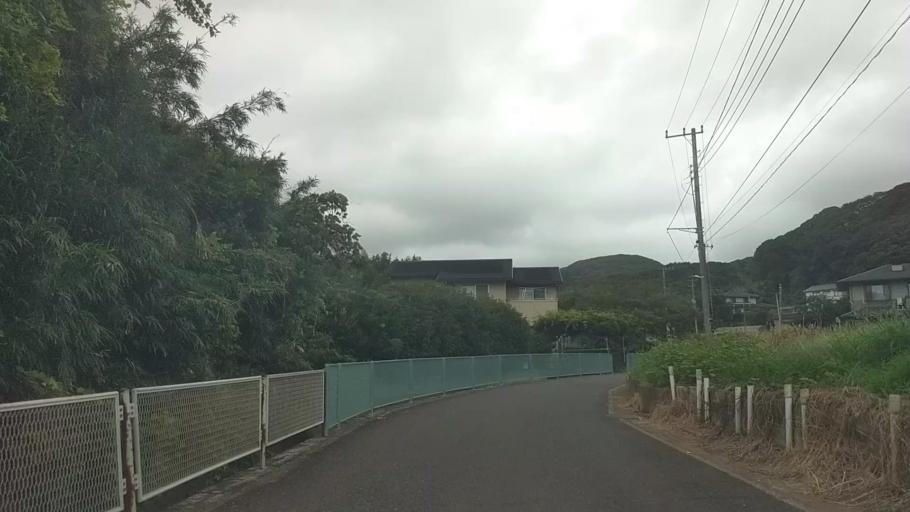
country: JP
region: Kanagawa
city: Hayama
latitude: 35.2314
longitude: 139.6239
